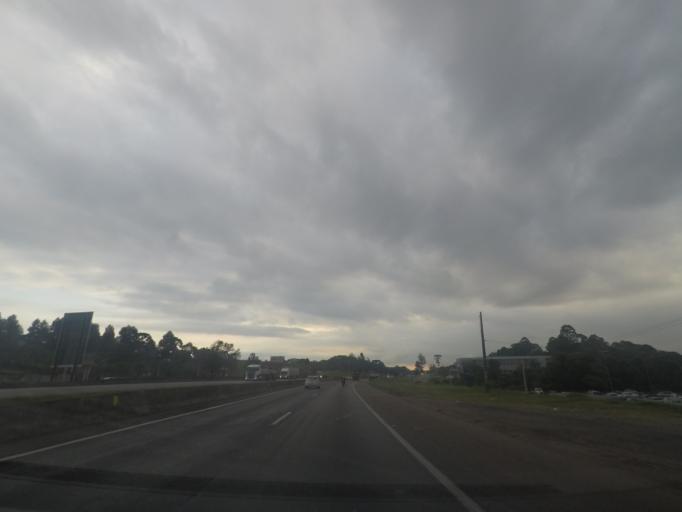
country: BR
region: Parana
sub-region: Sao Jose Dos Pinhais
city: Sao Jose dos Pinhais
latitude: -25.5720
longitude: -49.2000
